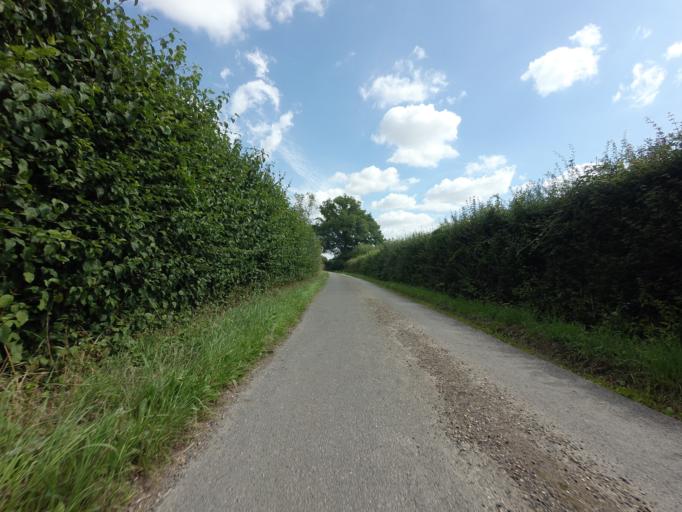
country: GB
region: England
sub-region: Kent
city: Tenterden
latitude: 51.0685
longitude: 0.7254
